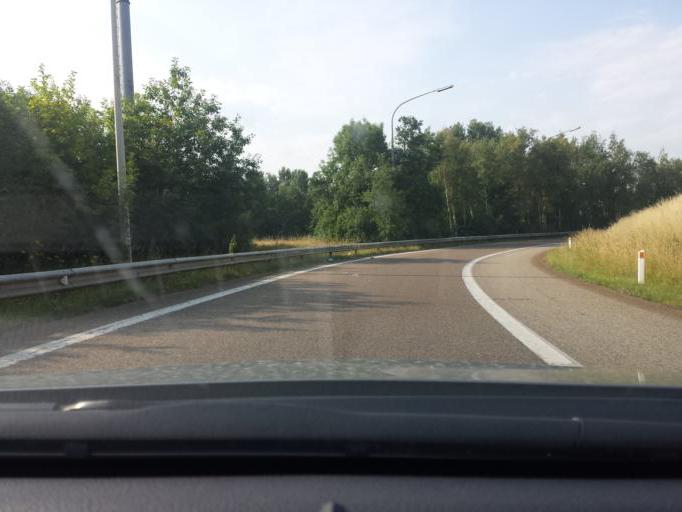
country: BE
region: Flanders
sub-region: Provincie Limburg
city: Tongeren
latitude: 50.7913
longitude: 5.5326
